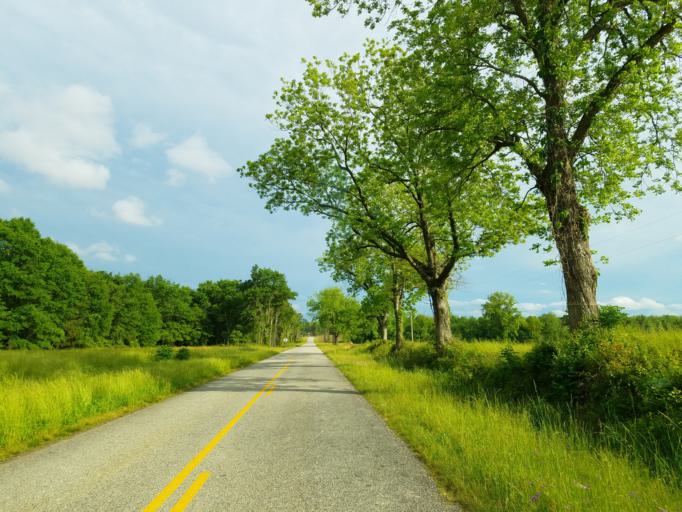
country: US
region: Georgia
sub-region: Dooly County
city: Vienna
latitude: 32.1667
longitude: -83.7647
